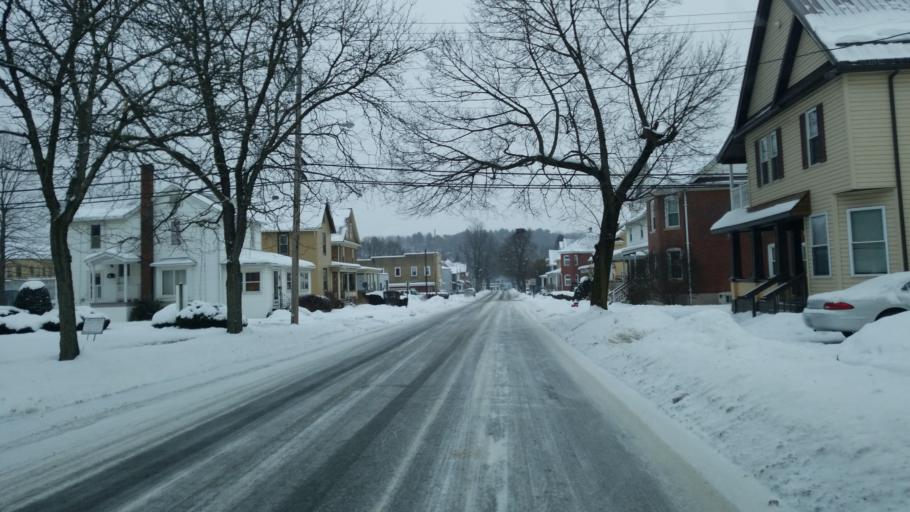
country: US
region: Pennsylvania
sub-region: Clearfield County
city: Clearfield
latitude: 41.0273
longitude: -78.4447
